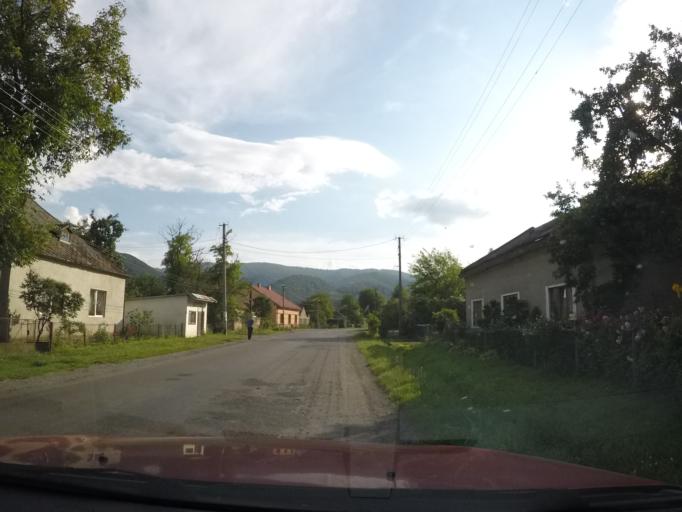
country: UA
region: Zakarpattia
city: Velykyi Bereznyi
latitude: 48.9442
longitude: 22.5975
